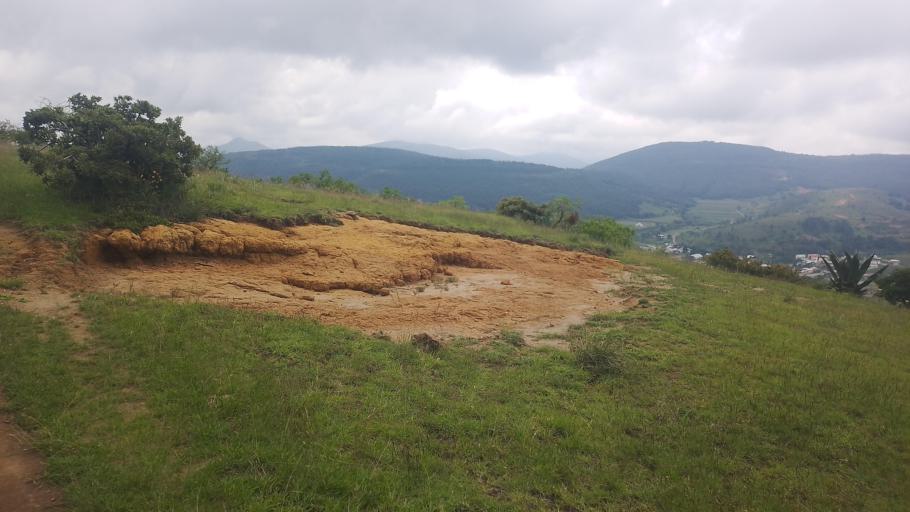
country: MX
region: Puebla
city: Santa Maria Malacatepec
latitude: 18.9321
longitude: -98.3191
